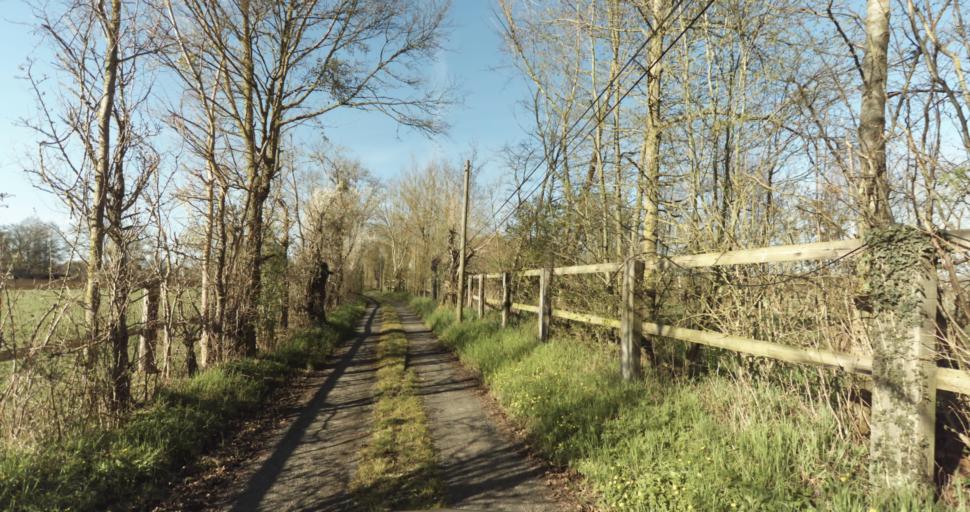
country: FR
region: Lower Normandy
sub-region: Departement du Calvados
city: Saint-Pierre-sur-Dives
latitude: 49.0447
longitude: 0.0594
